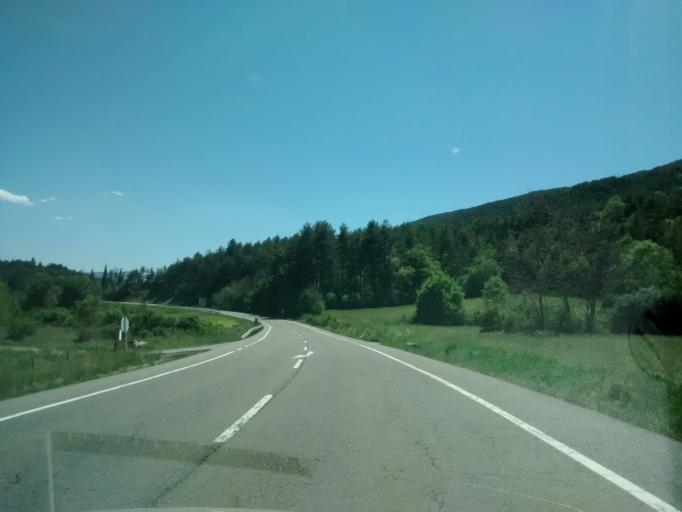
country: ES
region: Aragon
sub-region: Provincia de Huesca
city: Castiello de Jaca
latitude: 42.6543
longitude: -0.5589
